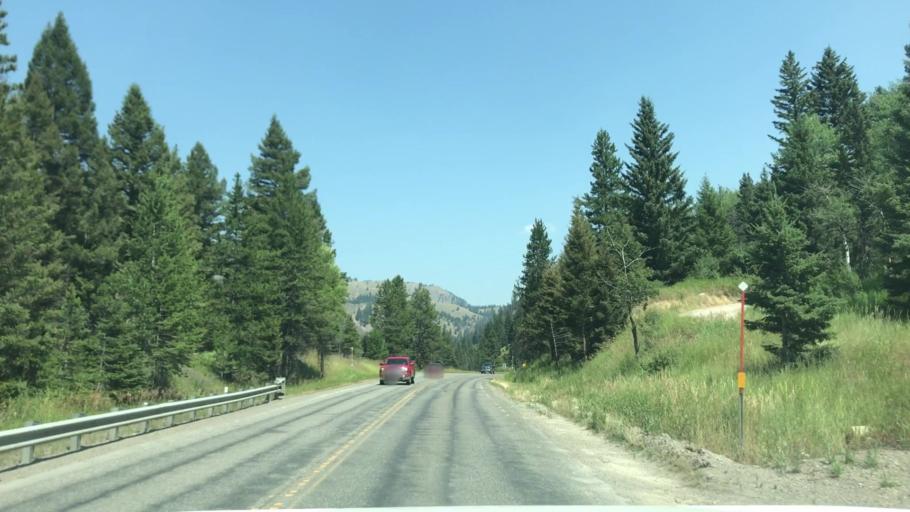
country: US
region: Montana
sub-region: Gallatin County
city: Big Sky
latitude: 45.2823
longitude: -111.2253
